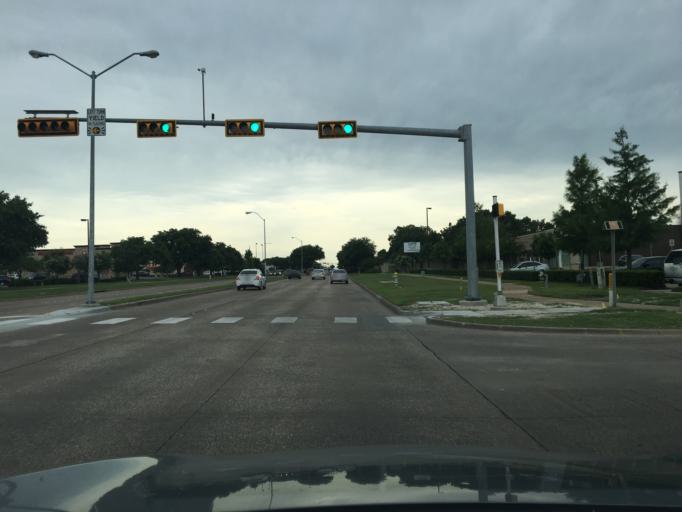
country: US
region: Texas
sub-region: Dallas County
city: Richardson
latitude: 32.9432
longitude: -96.7000
